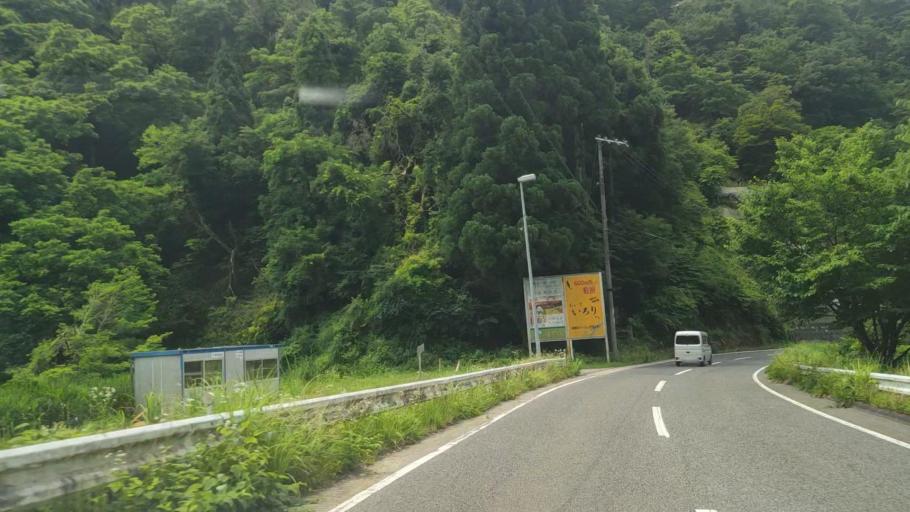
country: JP
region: Hyogo
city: Toyooka
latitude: 35.4801
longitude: 134.6126
